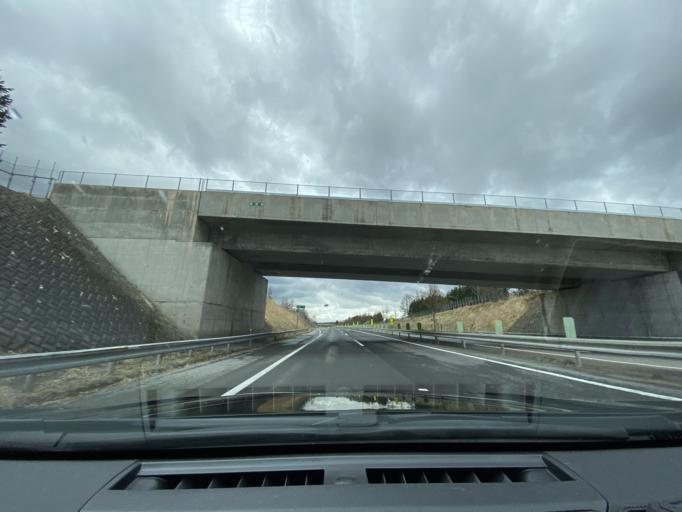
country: JP
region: Hokkaido
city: Takikawa
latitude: 43.6167
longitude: 141.9725
